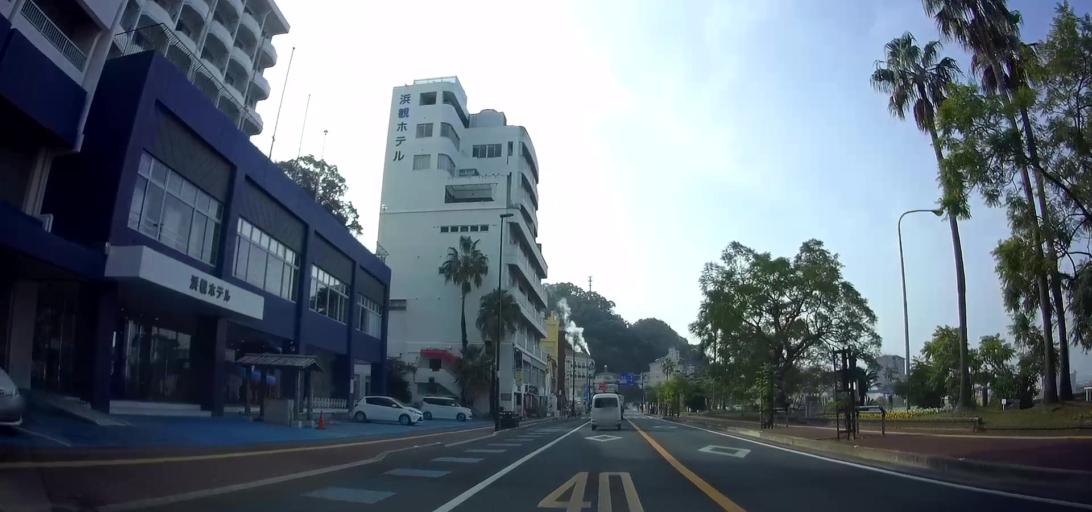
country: JP
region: Nagasaki
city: Shimabara
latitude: 32.7283
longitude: 130.2068
